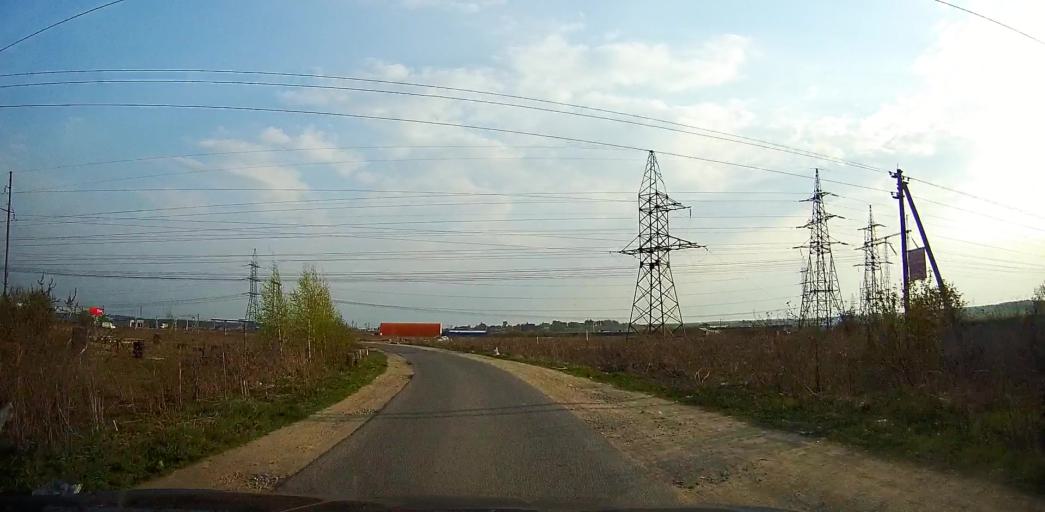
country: RU
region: Moskovskaya
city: Andreyevskoye
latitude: 55.5386
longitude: 37.9699
